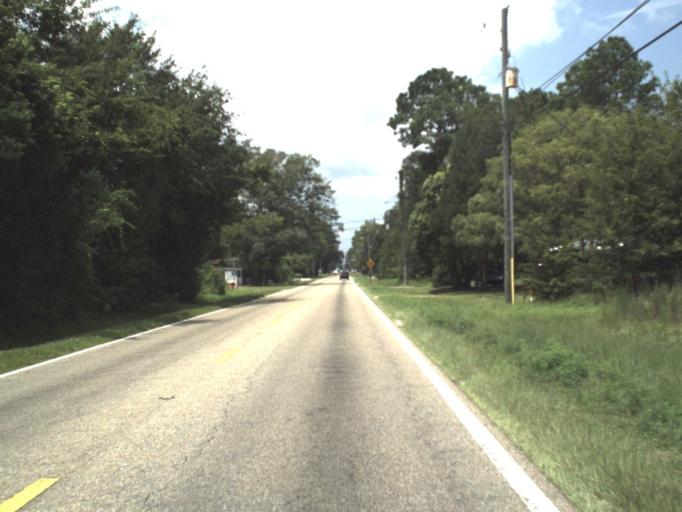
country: US
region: Florida
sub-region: Bay County
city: Lynn Haven
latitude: 30.2375
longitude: -85.6409
